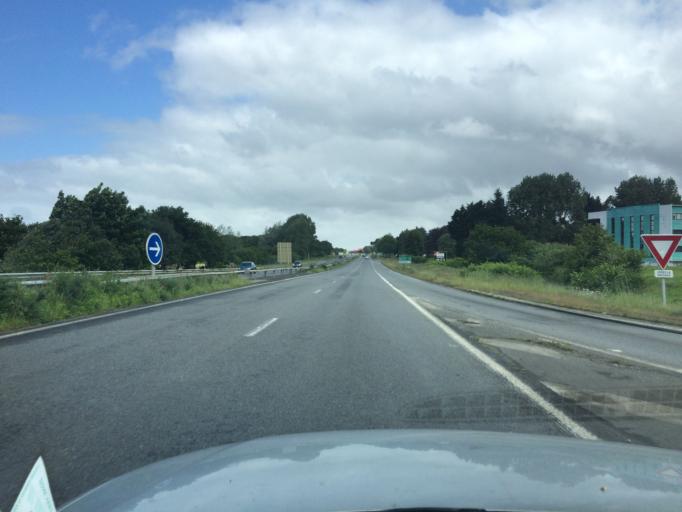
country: FR
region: Brittany
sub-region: Departement du Finistere
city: Gouesnou
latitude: 48.4333
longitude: -4.4641
